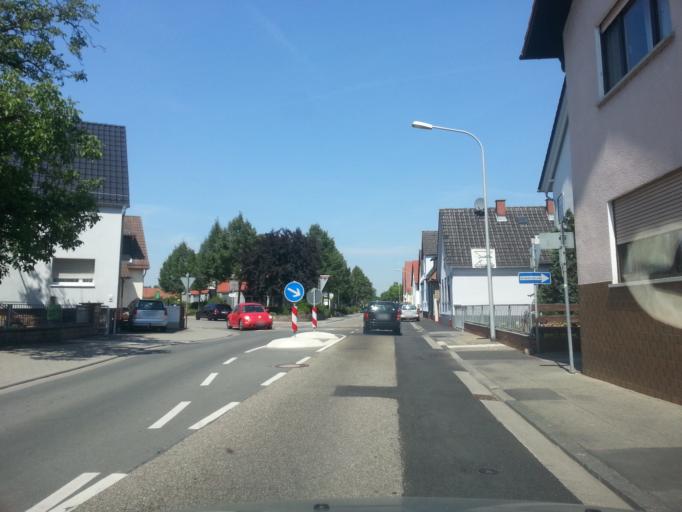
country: DE
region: Hesse
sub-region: Regierungsbezirk Darmstadt
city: Einhausen
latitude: 49.6748
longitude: 8.5408
